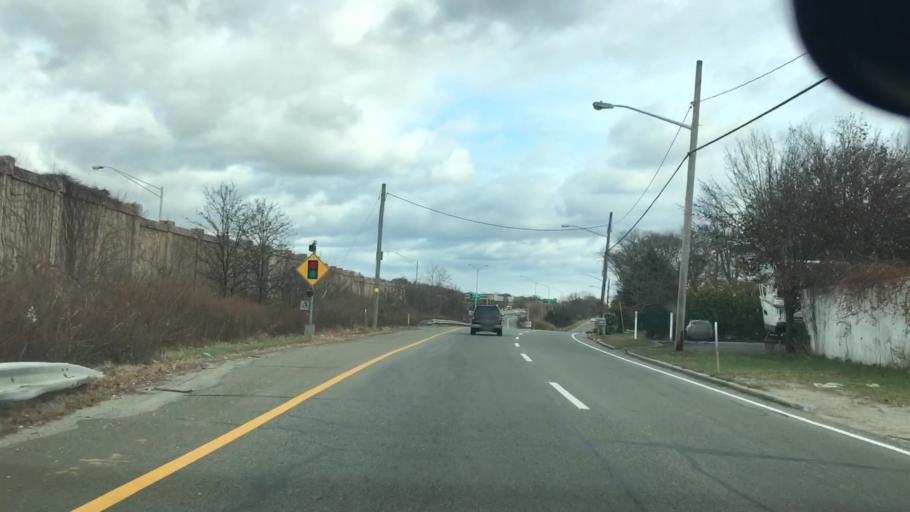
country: US
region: New York
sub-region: Suffolk County
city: Ronkonkoma
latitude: 40.8131
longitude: -73.1072
